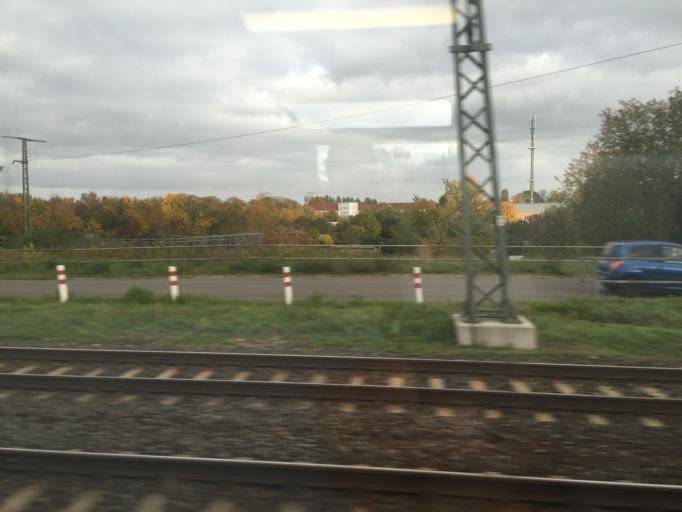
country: DE
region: Saxony
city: Leipzig
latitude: 51.3715
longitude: 12.3992
